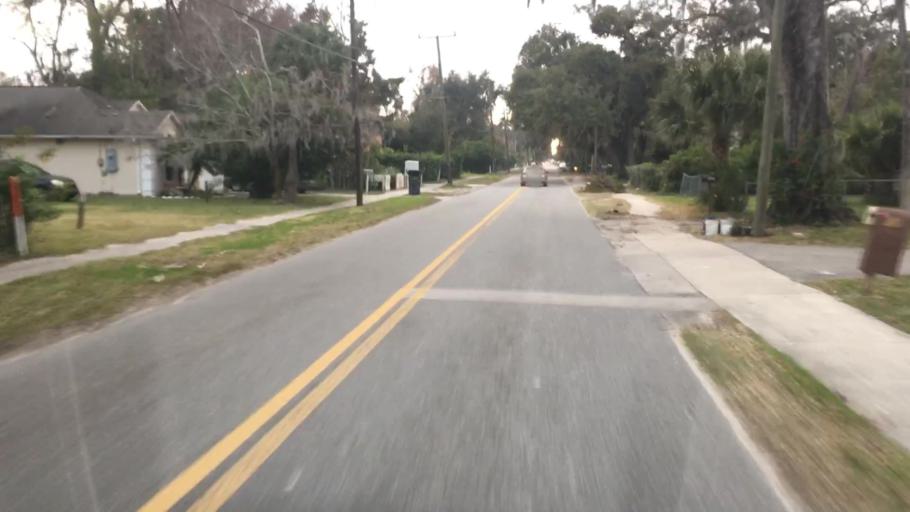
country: US
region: Florida
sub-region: Volusia County
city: Daytona Beach
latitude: 29.2208
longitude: -81.0362
